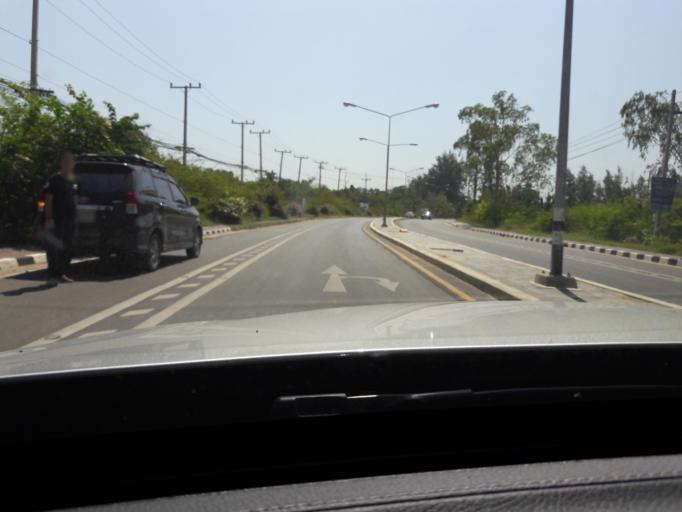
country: TH
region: Phetchaburi
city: Cha-am
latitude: 12.8139
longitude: 99.9812
